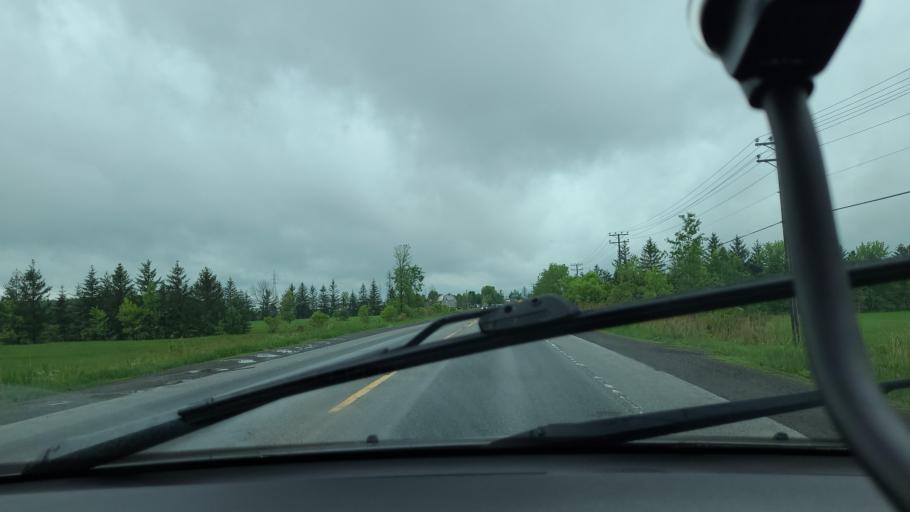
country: CA
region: Quebec
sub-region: Laurentides
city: Saint-Jerome
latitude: 45.7373
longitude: -74.0382
